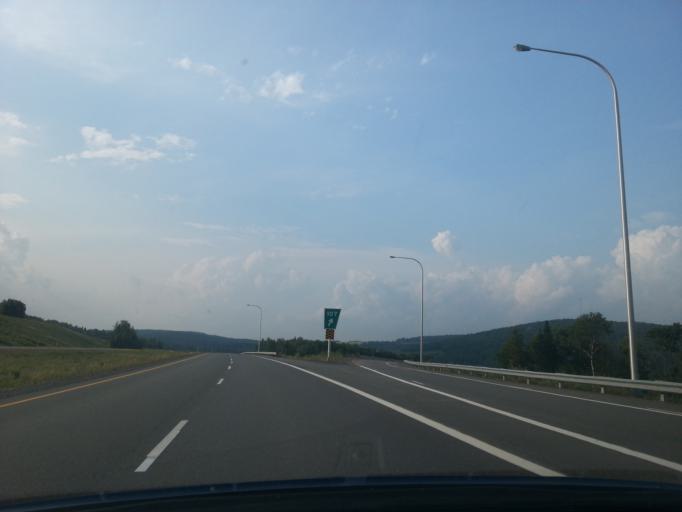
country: US
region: Maine
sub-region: Aroostook County
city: Fort Fairfield
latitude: 46.8111
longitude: -67.7293
